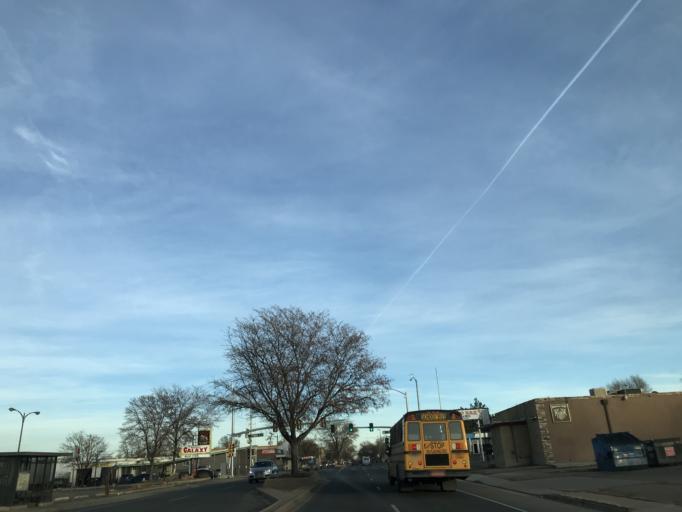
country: US
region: Colorado
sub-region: Adams County
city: Aurora
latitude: 39.7474
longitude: -104.8787
